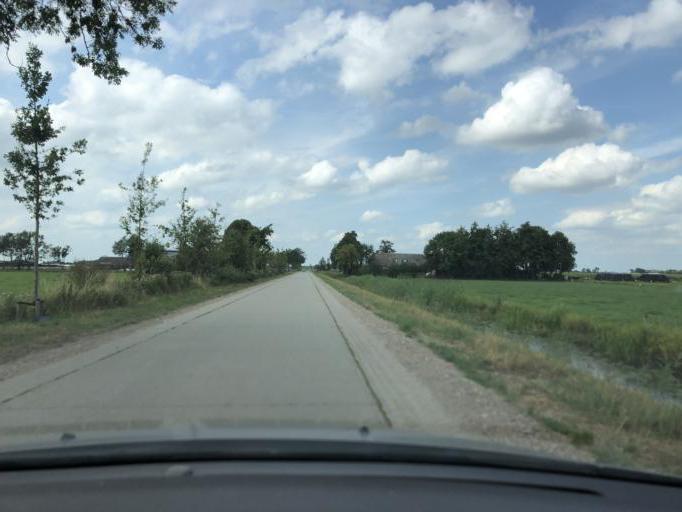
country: NL
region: Overijssel
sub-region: Gemeente Dalfsen
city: Dalfsen
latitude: 52.5627
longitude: 6.2025
